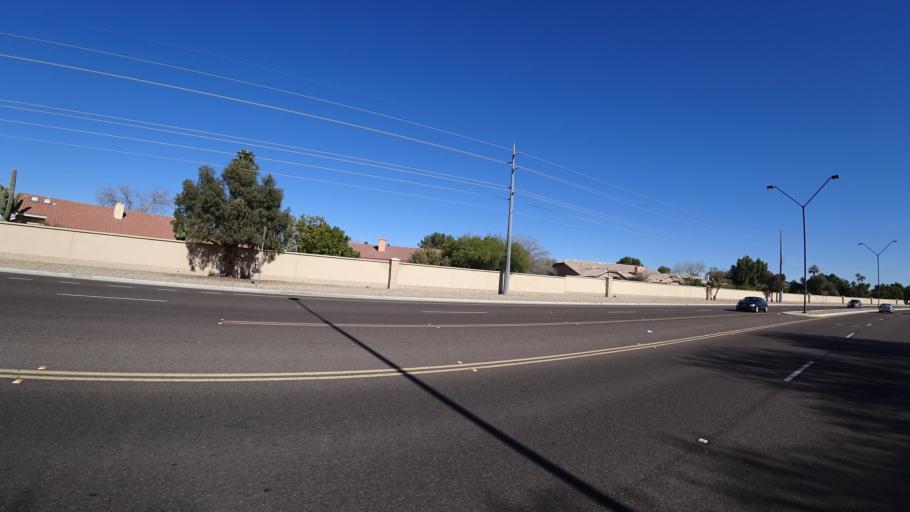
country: US
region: Arizona
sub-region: Maricopa County
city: Litchfield Park
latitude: 33.4925
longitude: -112.3451
